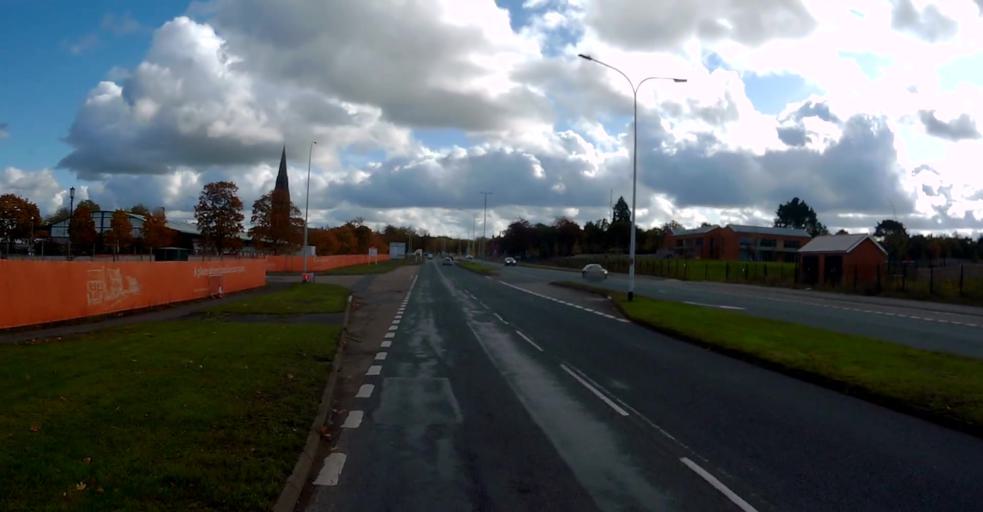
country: GB
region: England
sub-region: Hampshire
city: Aldershot
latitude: 51.2606
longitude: -0.7636
